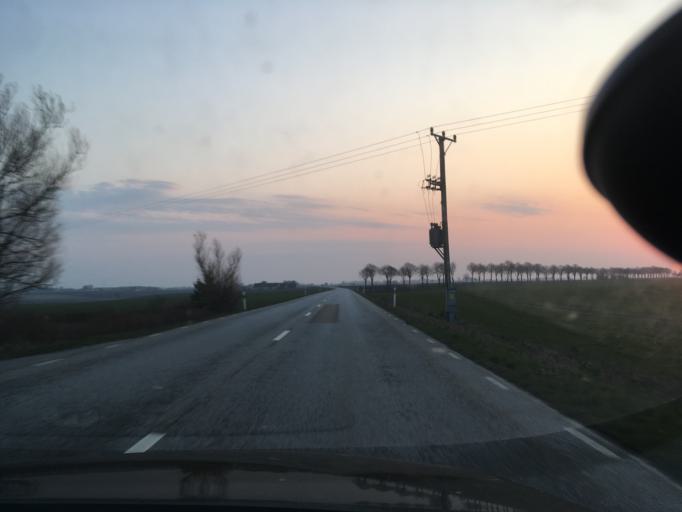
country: SE
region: Skane
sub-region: Ystads Kommun
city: Kopingebro
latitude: 55.4691
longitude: 14.0438
